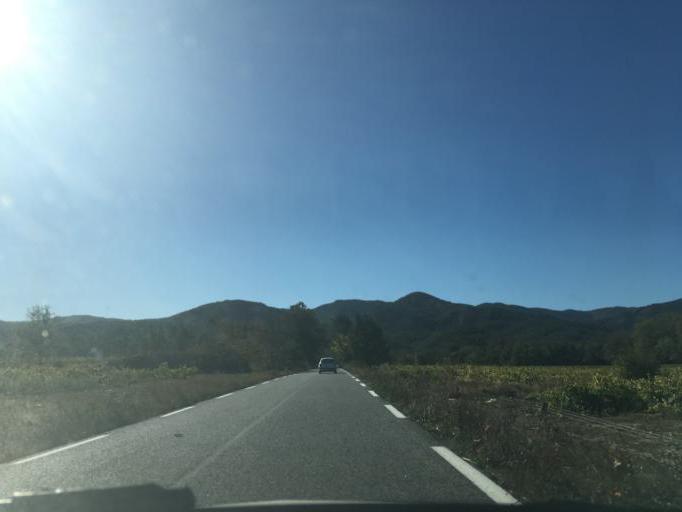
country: FR
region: Provence-Alpes-Cote d'Azur
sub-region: Departement du Var
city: La Garde-Freinet
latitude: 43.3393
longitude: 6.4276
